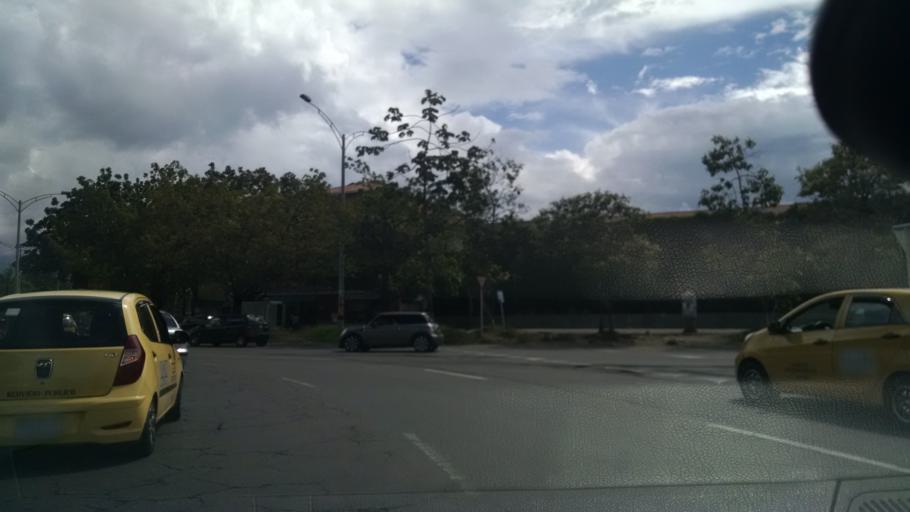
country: CO
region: Antioquia
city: Itagui
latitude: 6.2174
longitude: -75.5864
